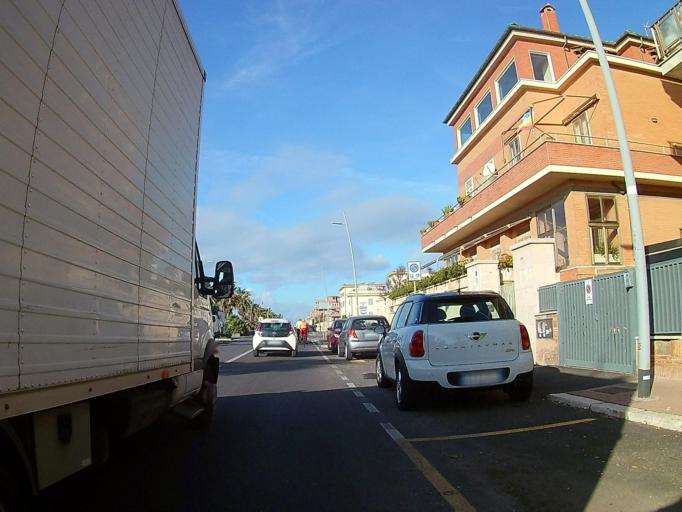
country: IT
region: Latium
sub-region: Citta metropolitana di Roma Capitale
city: Lido di Ostia
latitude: 41.7324
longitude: 12.2681
